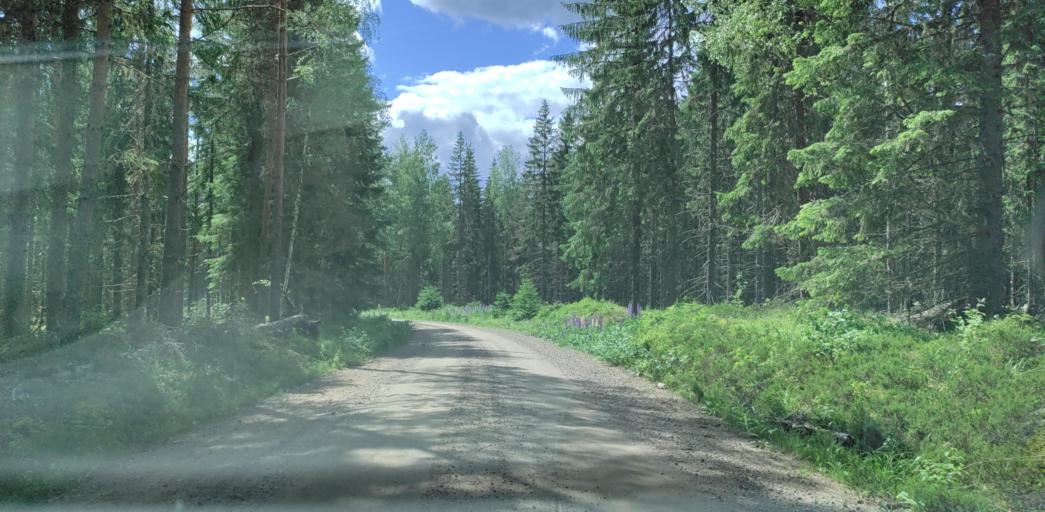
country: SE
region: Vaermland
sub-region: Hagfors Kommun
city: Ekshaerad
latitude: 60.0680
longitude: 13.3081
